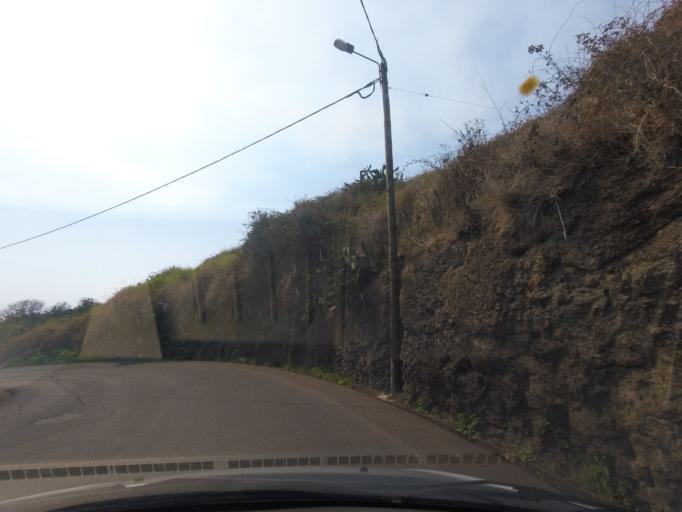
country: PT
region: Madeira
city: Ribeira Brava
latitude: 32.6828
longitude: -17.0695
